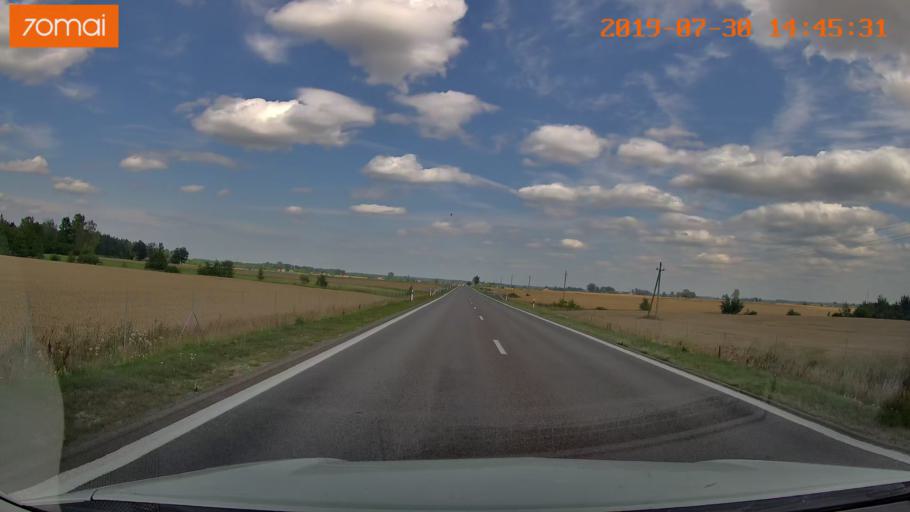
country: LT
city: Prienai
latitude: 54.5765
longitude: 23.7831
